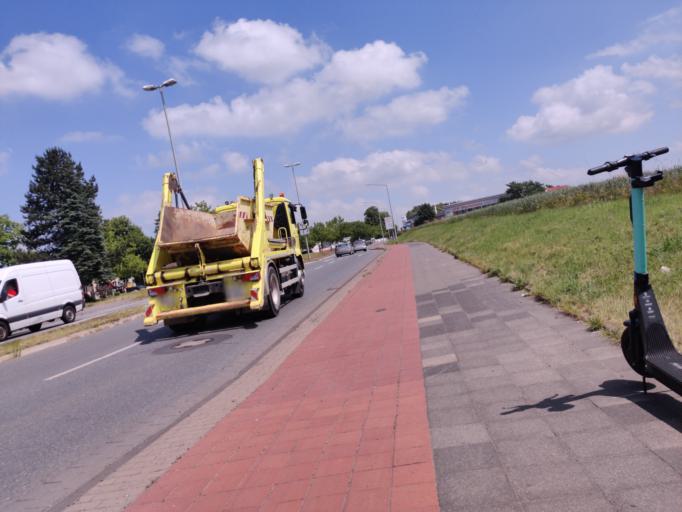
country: DE
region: Lower Saxony
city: Hildesheim
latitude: 52.1713
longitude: 9.9355
